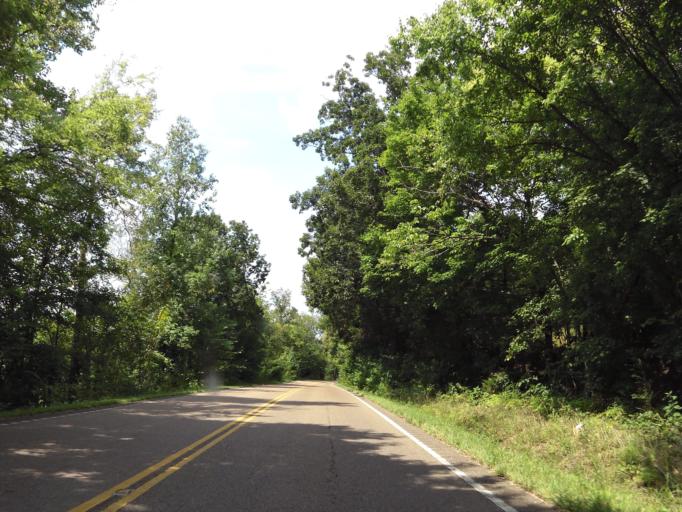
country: US
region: Tennessee
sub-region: Perry County
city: Linden
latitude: 35.6218
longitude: -87.9303
